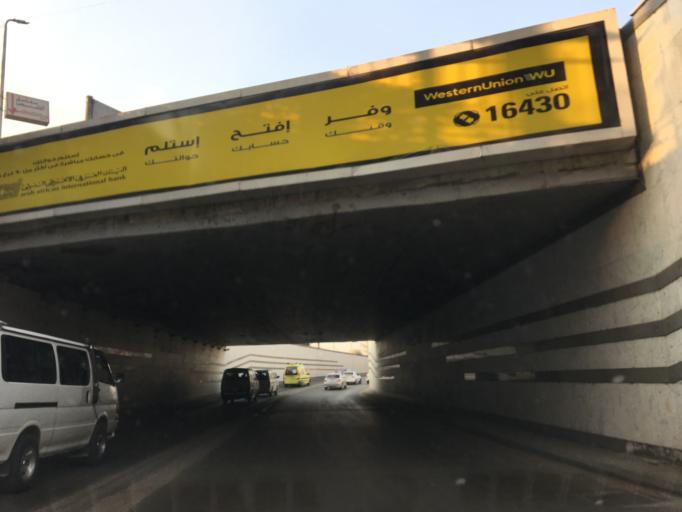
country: EG
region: Muhafazat al Qahirah
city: Cairo
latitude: 30.0438
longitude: 31.2322
